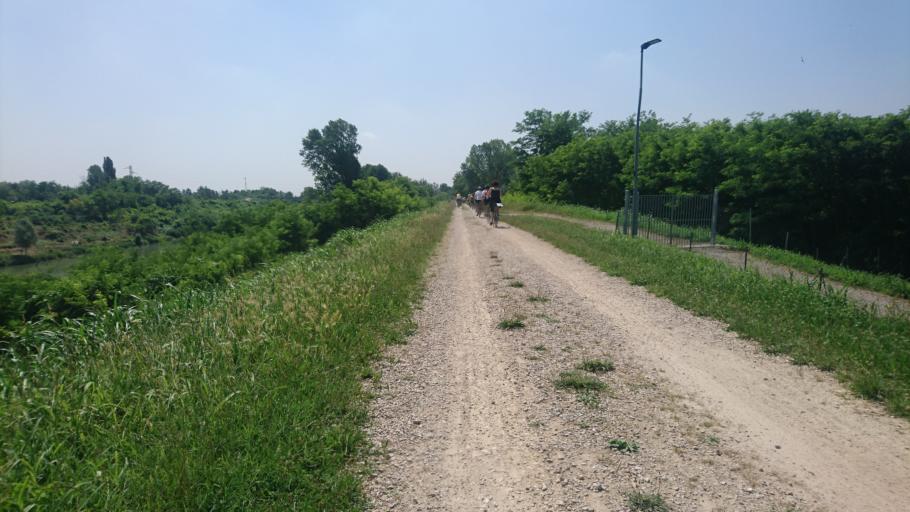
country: IT
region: Veneto
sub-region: Provincia di Venezia
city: Vigonovo
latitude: 45.3952
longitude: 12.0078
